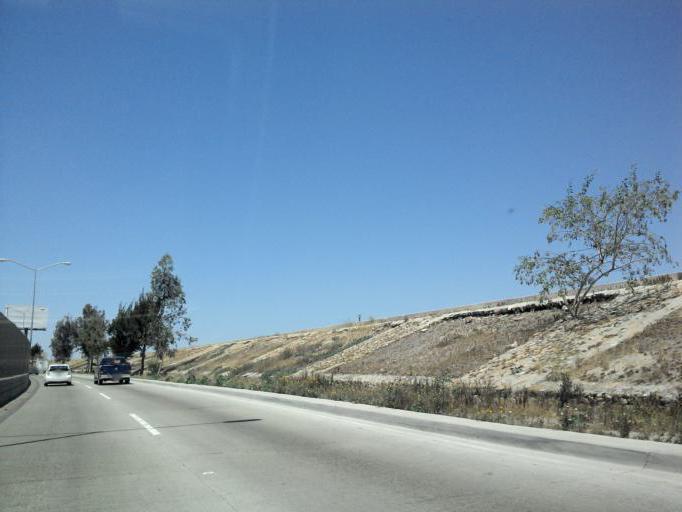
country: MX
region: Baja California
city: Tijuana
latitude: 32.5408
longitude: -117.0375
